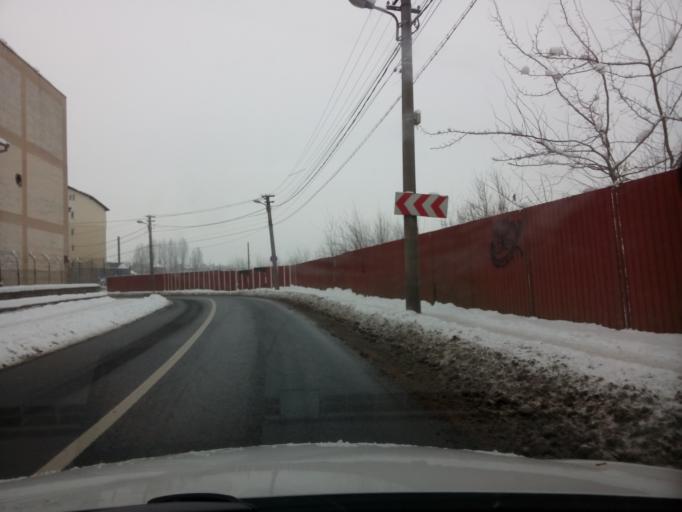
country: RO
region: Sibiu
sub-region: Municipiul Sibiu
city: Sibiu
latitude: 45.8031
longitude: 24.1563
